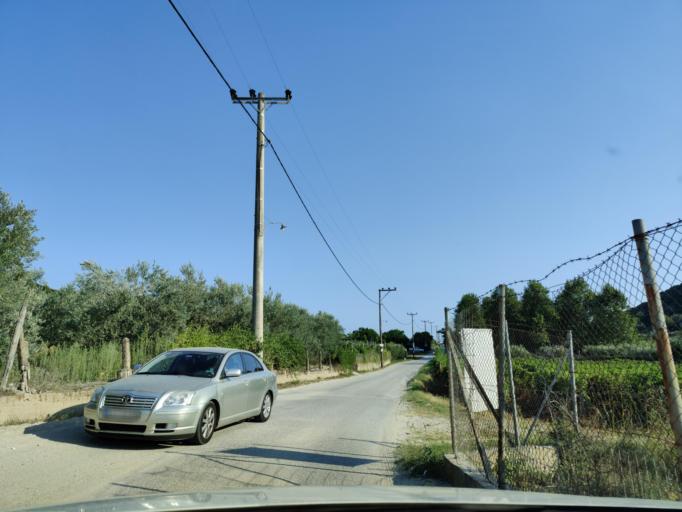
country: GR
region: East Macedonia and Thrace
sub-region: Nomos Kavalas
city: Nea Peramos
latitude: 40.8235
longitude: 24.3077
